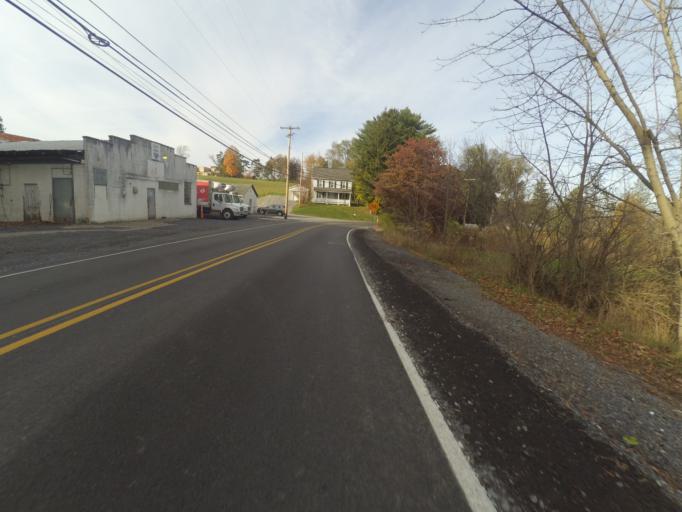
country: US
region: Pennsylvania
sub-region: Centre County
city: Houserville
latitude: 40.8132
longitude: -77.8388
